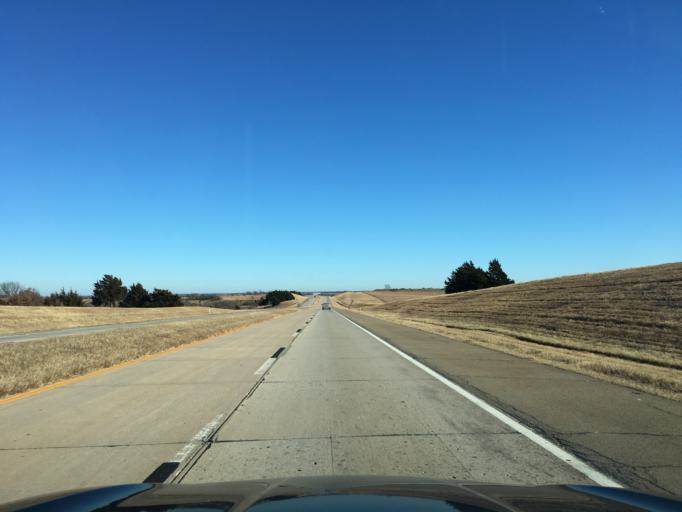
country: US
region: Oklahoma
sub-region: Payne County
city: Yale
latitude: 36.2240
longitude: -96.7416
